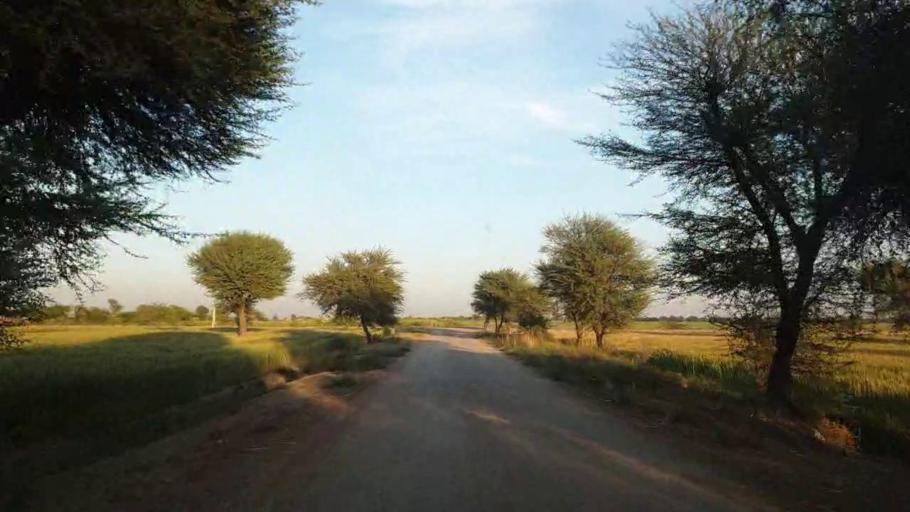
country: PK
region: Sindh
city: Kunri
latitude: 25.1288
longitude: 69.4410
